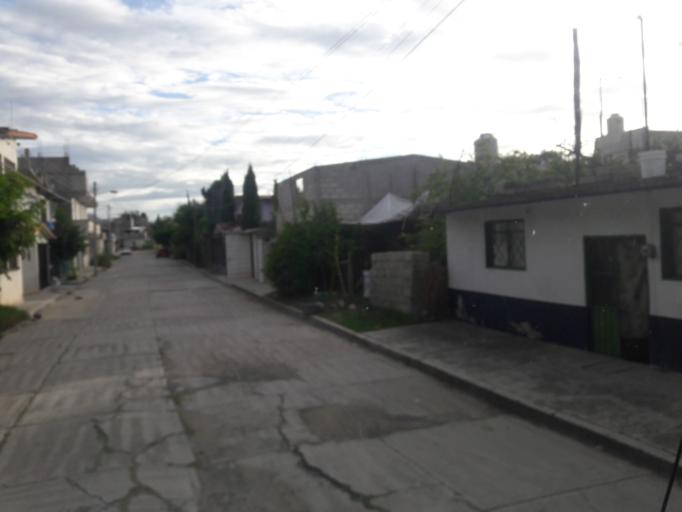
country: MX
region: Oaxaca
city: Ciudad de Huajuapam de Leon
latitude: 17.8029
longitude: -97.7861
